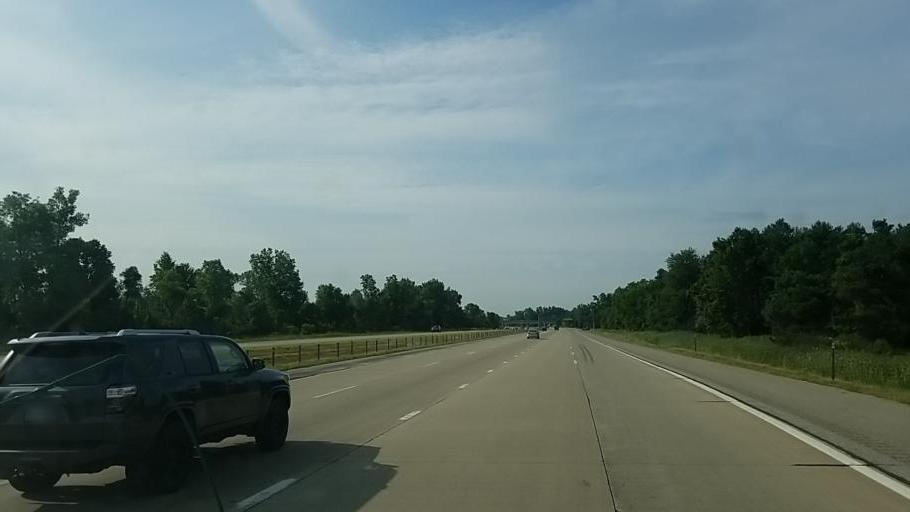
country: US
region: Michigan
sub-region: Eaton County
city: Dimondale
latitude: 42.6969
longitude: -84.6697
